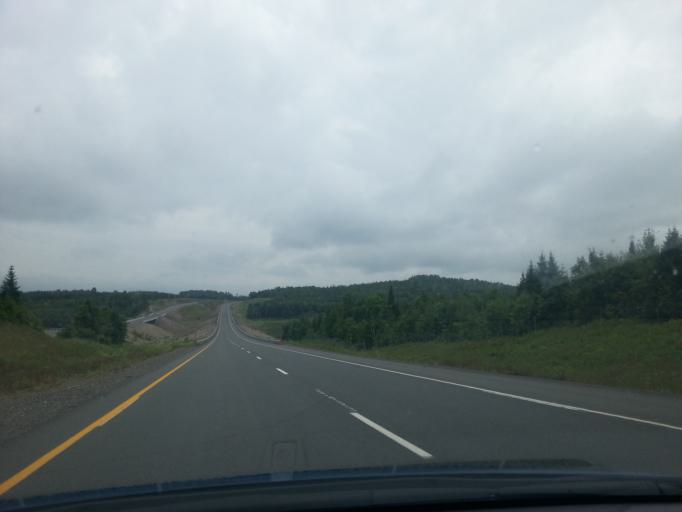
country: US
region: Maine
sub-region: Aroostook County
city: Easton
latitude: 46.5980
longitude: -67.7442
